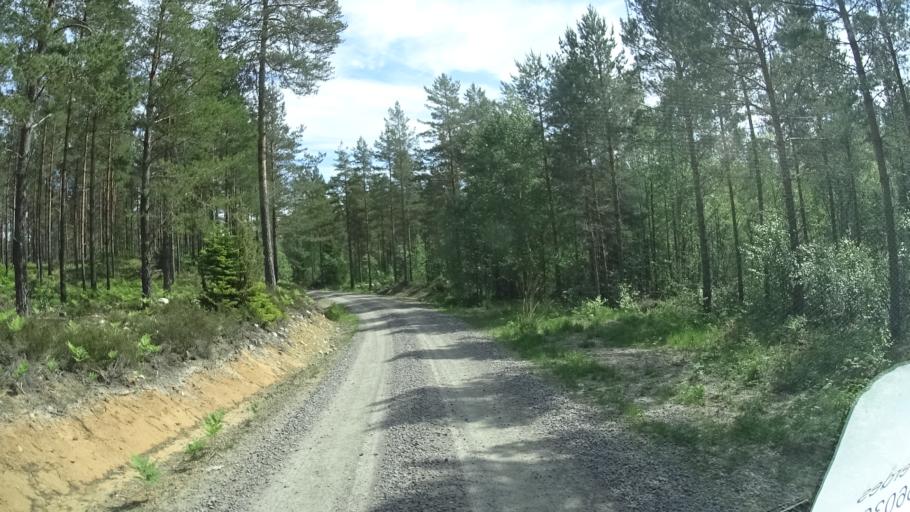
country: SE
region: OEstergoetland
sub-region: Norrkopings Kommun
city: Svartinge
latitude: 58.7709
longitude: 15.9577
